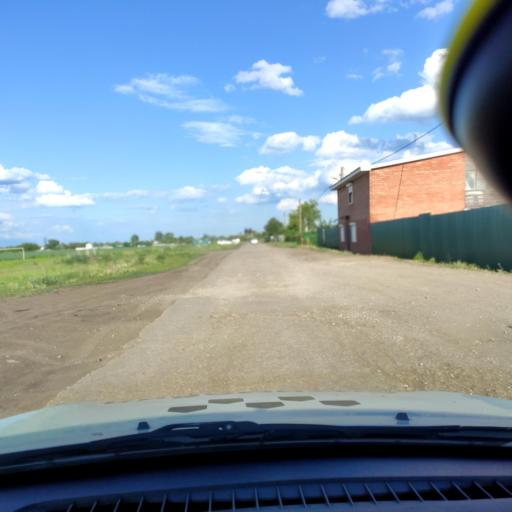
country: RU
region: Samara
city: Tol'yatti
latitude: 53.5906
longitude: 49.4447
